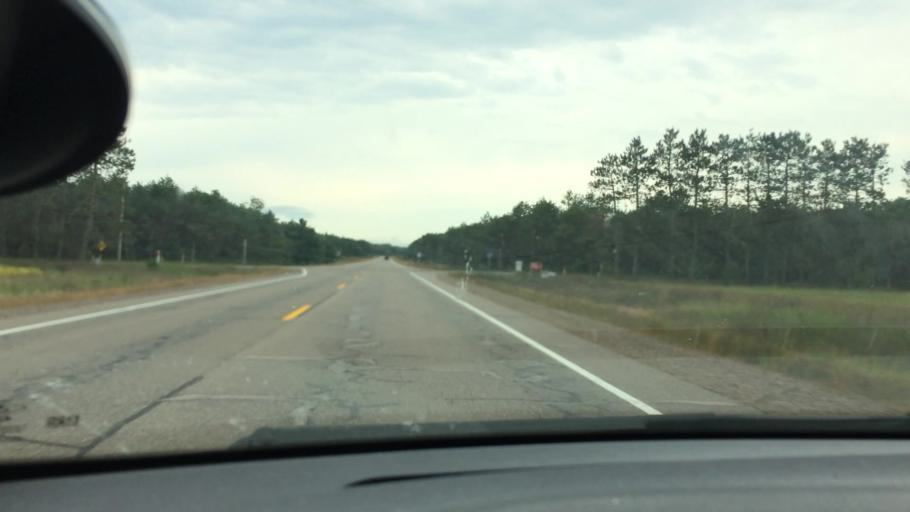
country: US
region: Wisconsin
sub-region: Eau Claire County
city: Augusta
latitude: 44.5804
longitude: -91.0639
